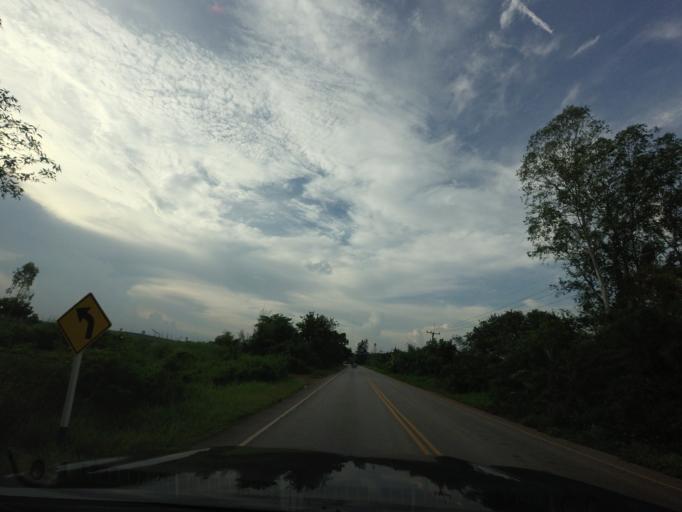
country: TH
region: Changwat Udon Thani
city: Nam Som
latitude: 17.8271
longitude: 102.2671
